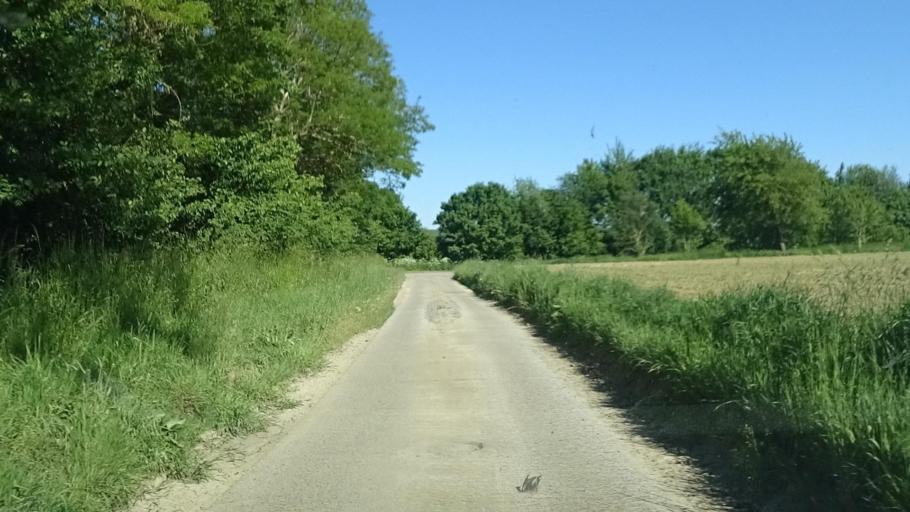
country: BE
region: Wallonia
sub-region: Province du Brabant Wallon
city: Walhain-Saint-Paul
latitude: 50.6547
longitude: 4.6808
